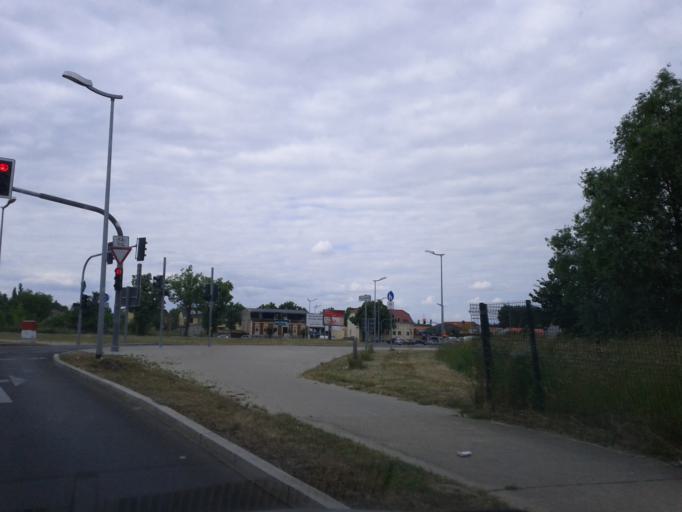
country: DE
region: Berlin
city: Hellersdorf
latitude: 52.5408
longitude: 13.6389
